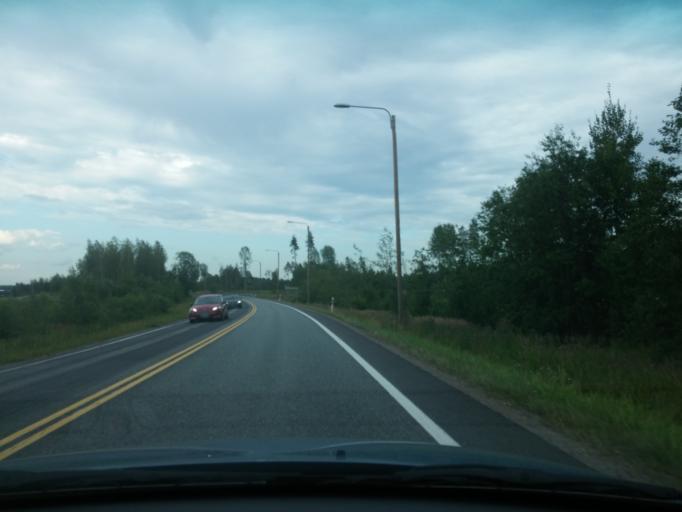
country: FI
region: Haeme
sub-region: Haemeenlinna
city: Tervakoski
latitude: 60.7415
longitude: 24.6768
